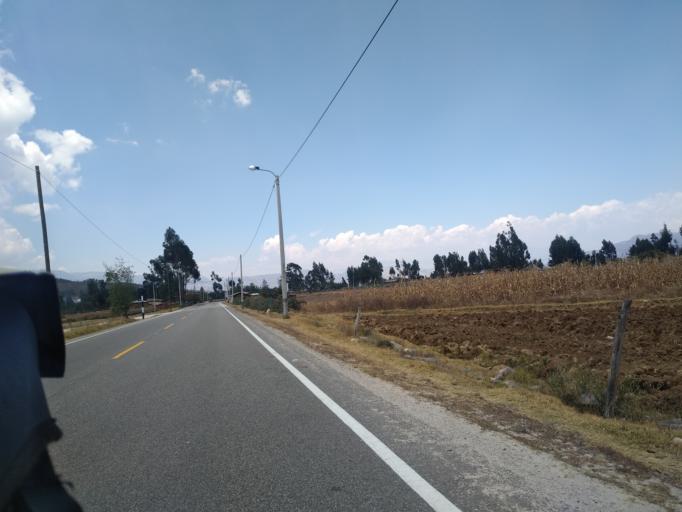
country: PE
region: Cajamarca
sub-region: San Marcos
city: San Marcos
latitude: -7.2815
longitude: -78.2288
